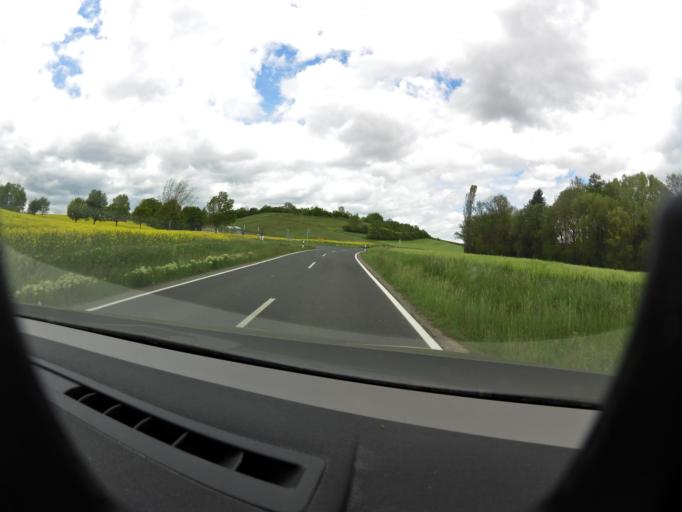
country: DE
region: Bavaria
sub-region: Regierungsbezirk Unterfranken
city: Dettelbach
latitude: 49.8218
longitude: 10.1494
